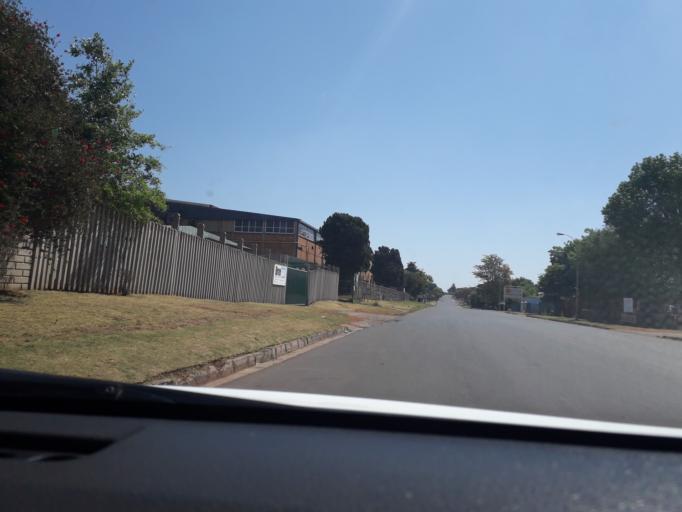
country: ZA
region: Gauteng
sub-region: City of Johannesburg Metropolitan Municipality
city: Modderfontein
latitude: -26.1135
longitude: 28.2211
